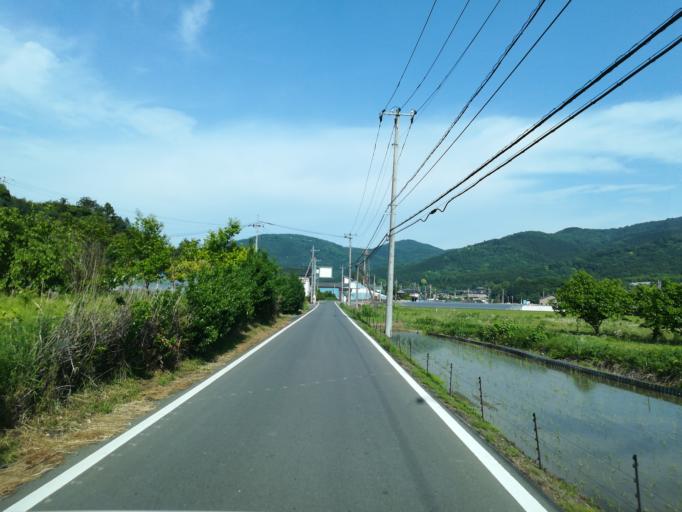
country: JP
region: Ibaraki
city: Tsukuba
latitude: 36.1890
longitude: 140.1655
